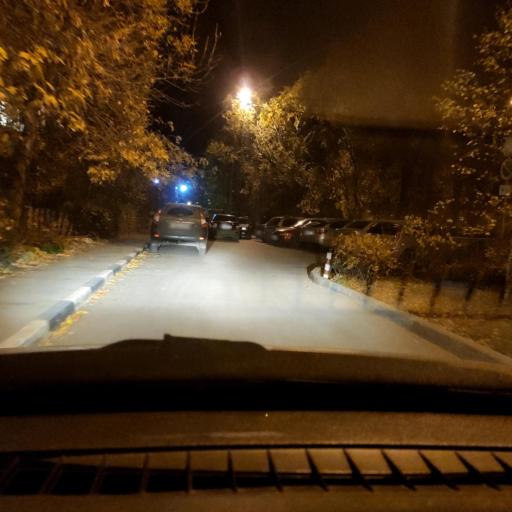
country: RU
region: Samara
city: Tol'yatti
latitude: 53.5334
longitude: 49.3040
